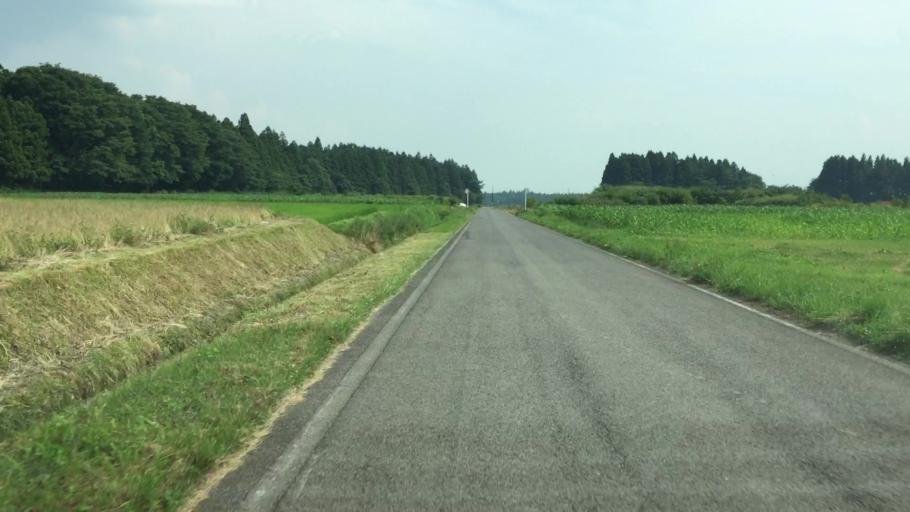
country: JP
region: Tochigi
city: Kuroiso
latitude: 37.0152
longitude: 139.9497
